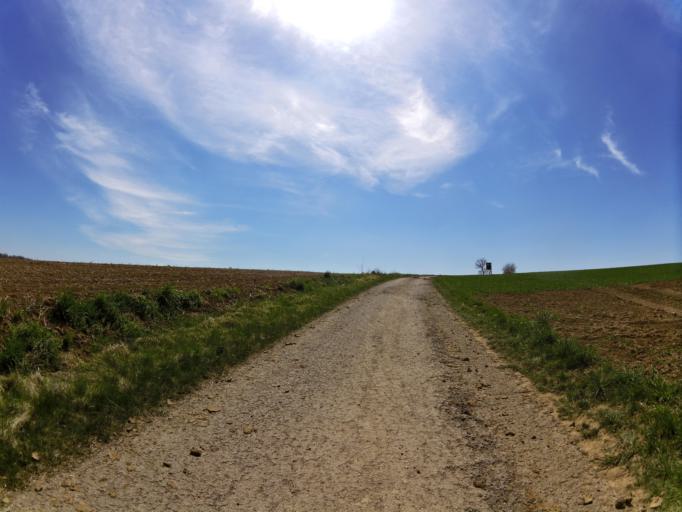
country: DE
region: Bavaria
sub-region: Regierungsbezirk Unterfranken
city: Winterhausen
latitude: 49.6973
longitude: 9.9963
